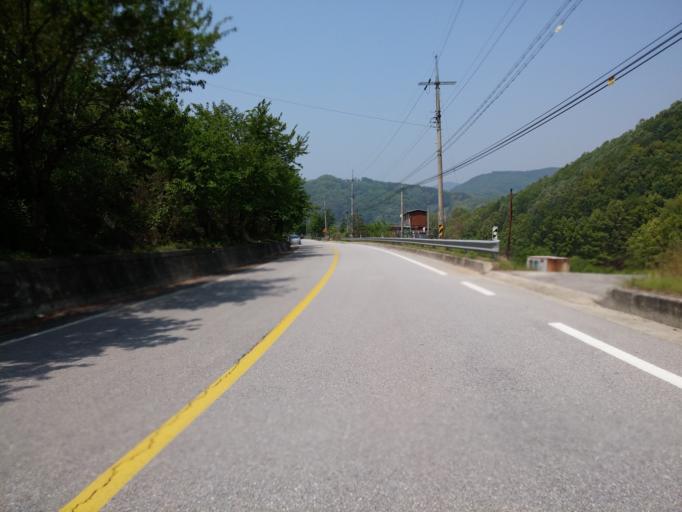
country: KR
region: Chungcheongbuk-do
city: Okcheon
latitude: 36.4305
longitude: 127.5773
